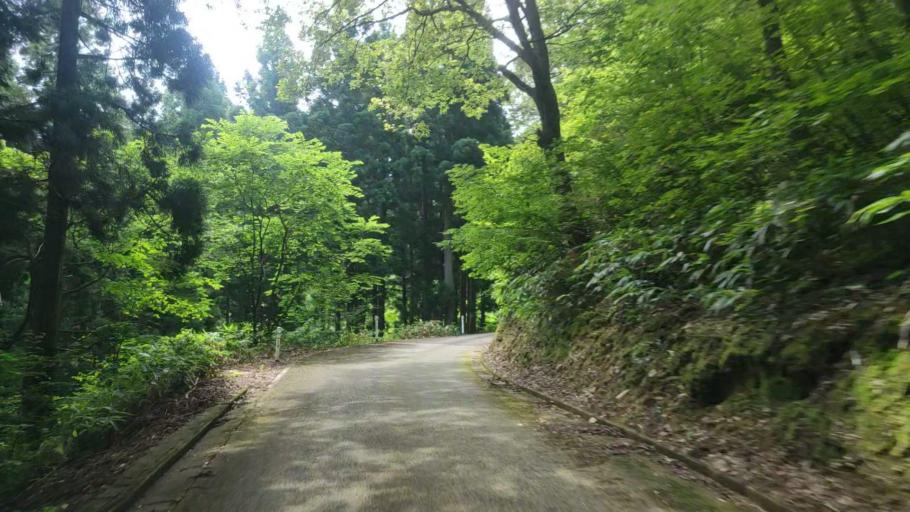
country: JP
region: Ishikawa
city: Komatsu
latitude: 36.2814
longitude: 136.5302
